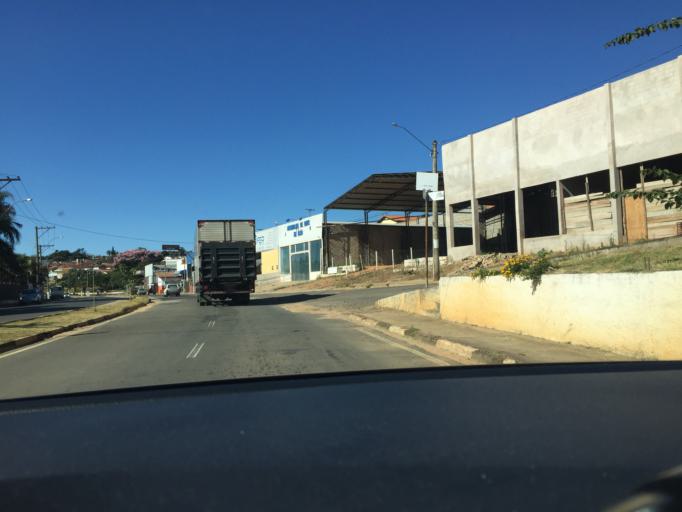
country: BR
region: Sao Paulo
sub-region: Santo Antonio Do Jardim
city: Espirito Santo do Pinhal
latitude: -22.1939
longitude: -46.7689
